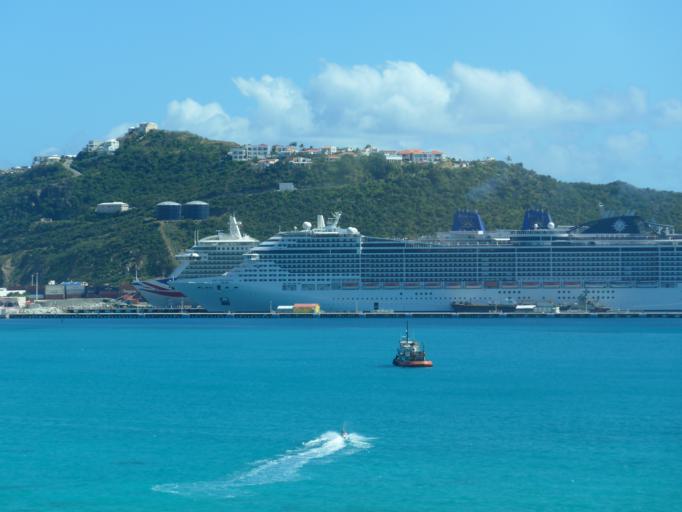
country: SX
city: Philipsburg
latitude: 18.0208
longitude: -63.0601
